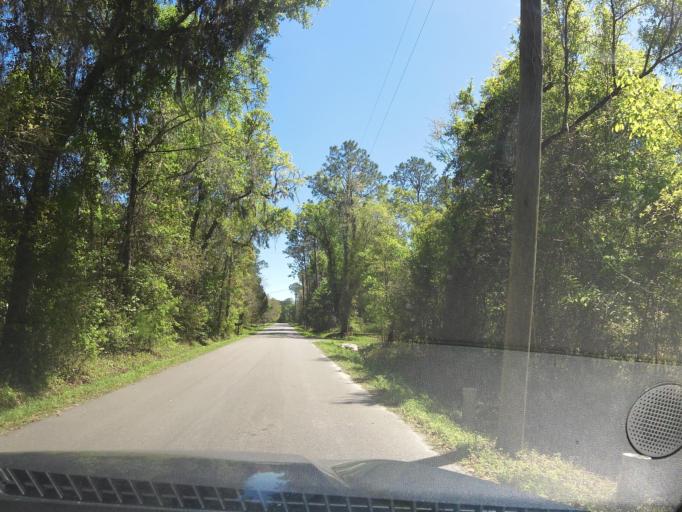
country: US
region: Florida
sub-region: Bradford County
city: Starke
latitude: 30.0490
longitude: -82.0683
